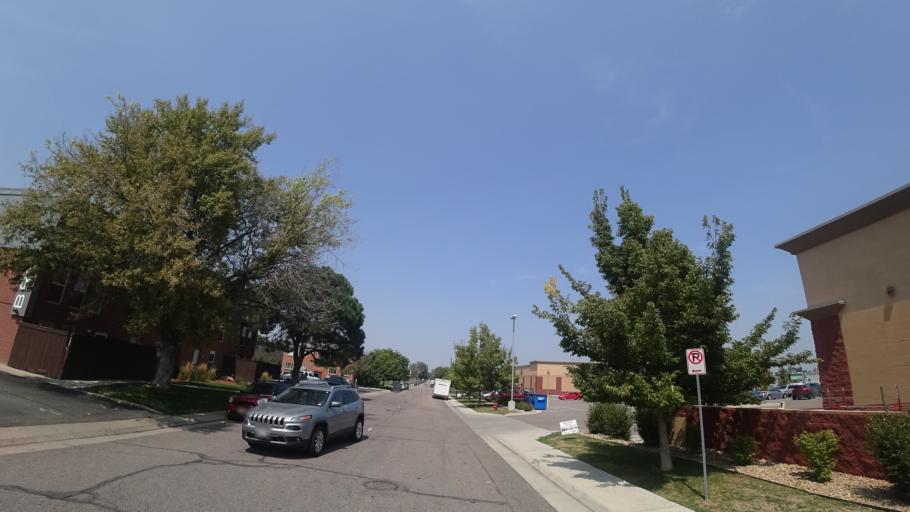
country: US
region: Colorado
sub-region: Arapahoe County
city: Englewood
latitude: 39.6247
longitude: -104.9891
